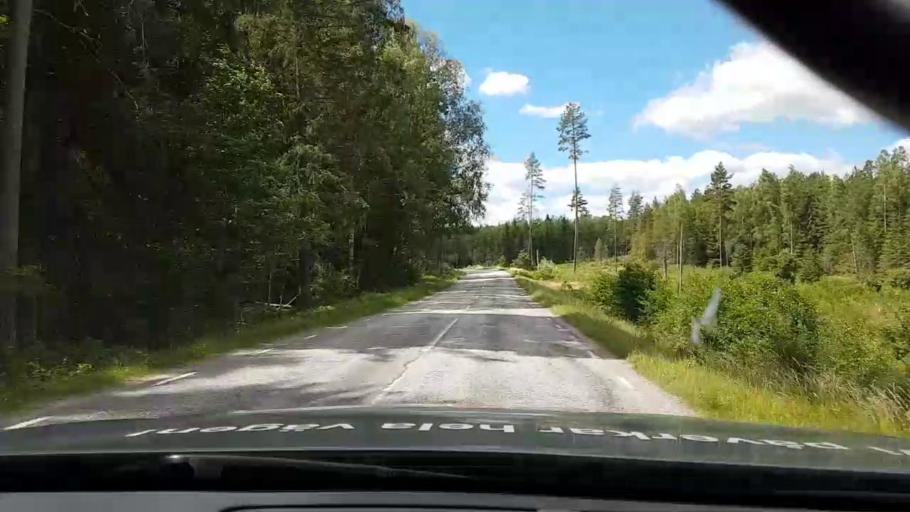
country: SE
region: Kalmar
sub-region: Vasterviks Kommun
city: Forserum
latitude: 58.0258
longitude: 16.5381
